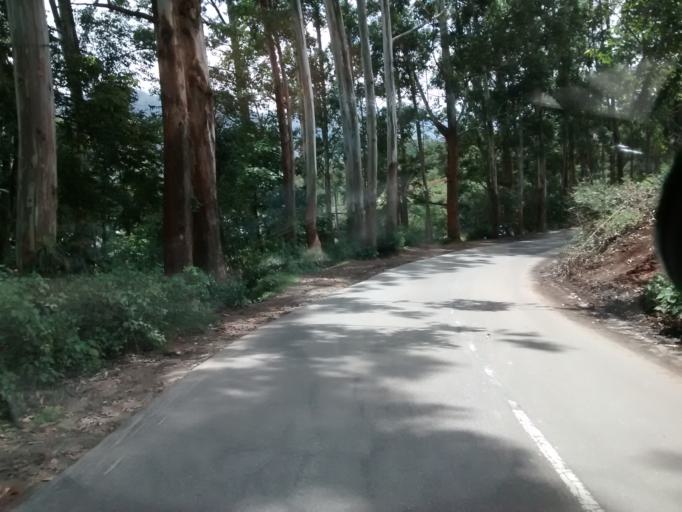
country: IN
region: Kerala
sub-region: Idukki
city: Munnar
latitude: 10.1057
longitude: 77.1280
